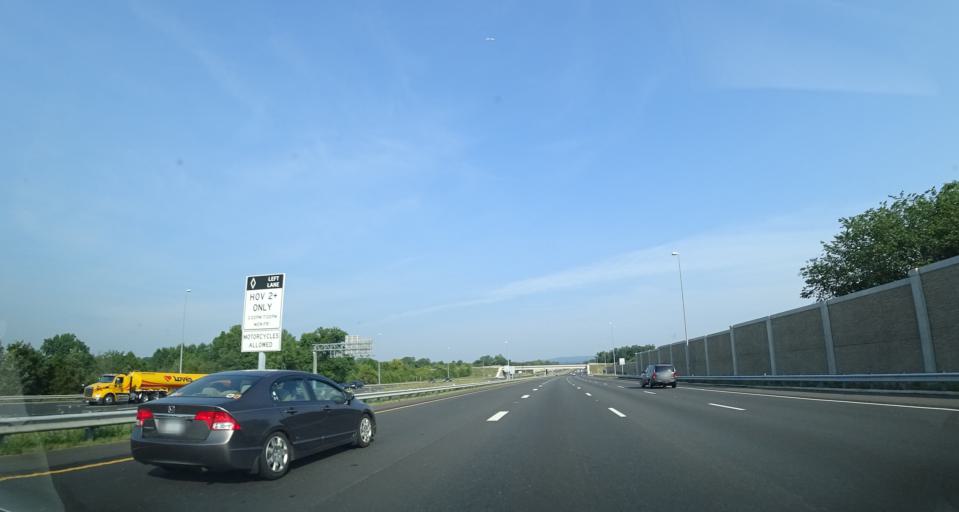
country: US
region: Virginia
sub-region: Prince William County
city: Gainesville
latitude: 38.8035
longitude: -77.6098
